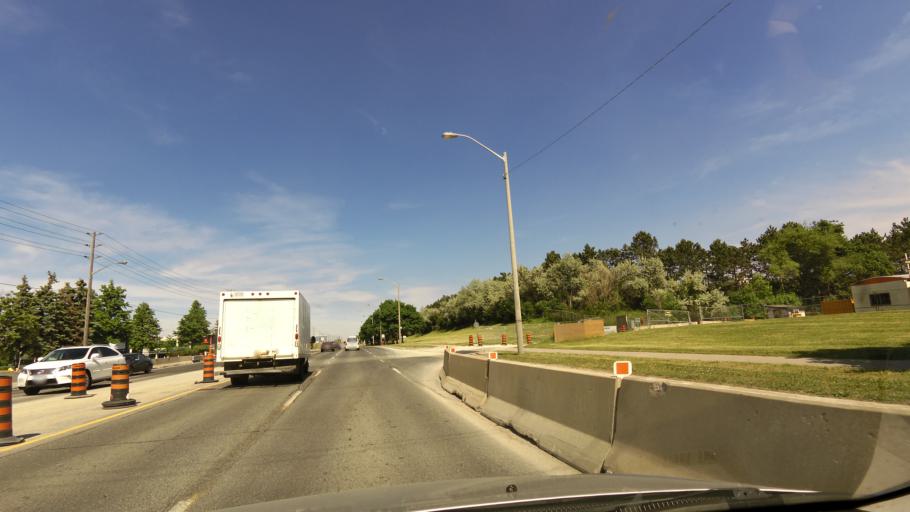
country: CA
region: Ontario
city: Concord
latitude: 43.7780
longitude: -79.5094
